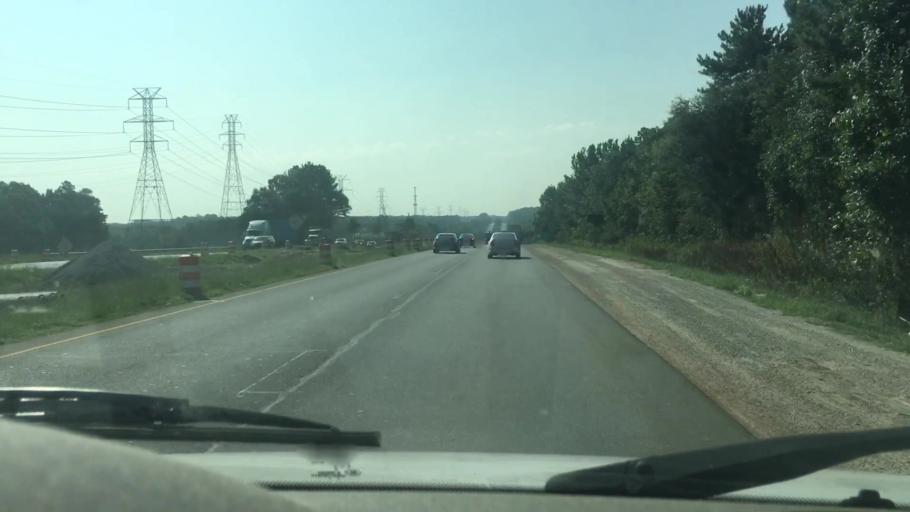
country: US
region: North Carolina
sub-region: Gaston County
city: Mount Holly
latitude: 35.3249
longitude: -80.9446
